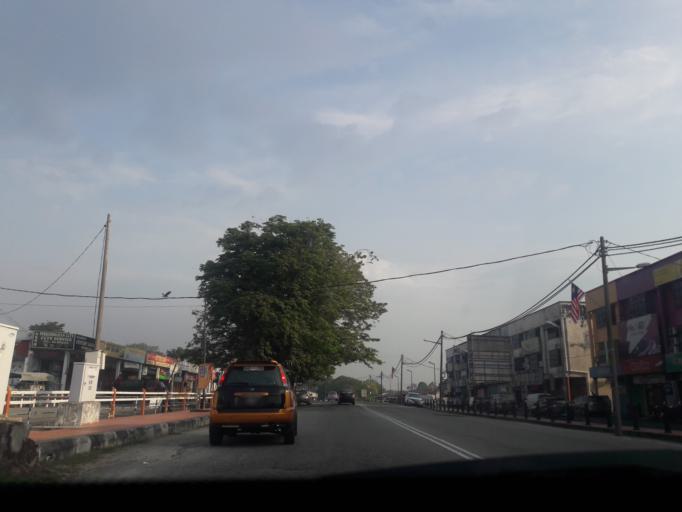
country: MY
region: Kedah
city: Kulim
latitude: 5.3768
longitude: 100.5393
